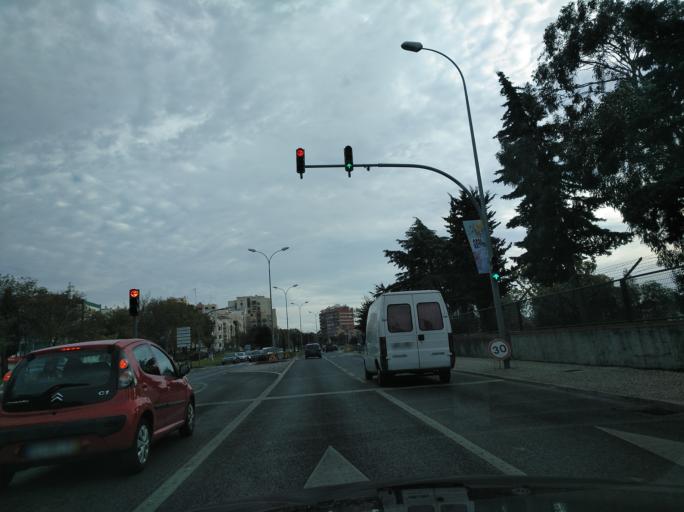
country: PT
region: Lisbon
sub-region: Amadora
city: Amadora
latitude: 38.7522
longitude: -9.2341
